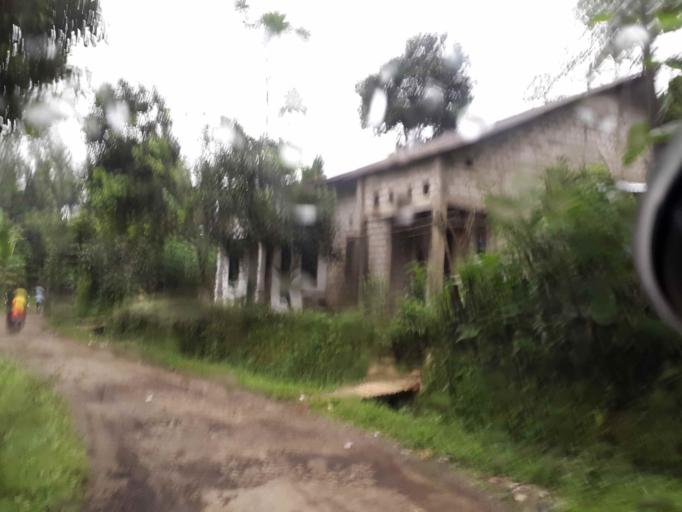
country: ID
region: Central Java
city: Lebaksiu
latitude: -7.1333
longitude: 109.2113
